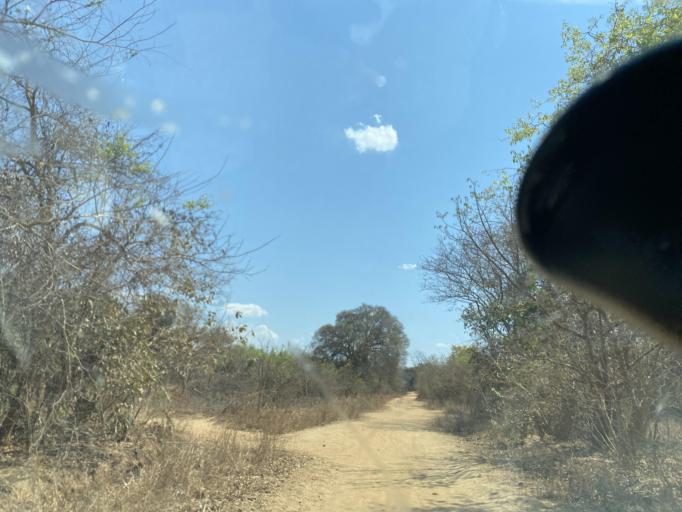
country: ZM
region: Lusaka
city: Chongwe
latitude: -15.0853
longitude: 29.4988
